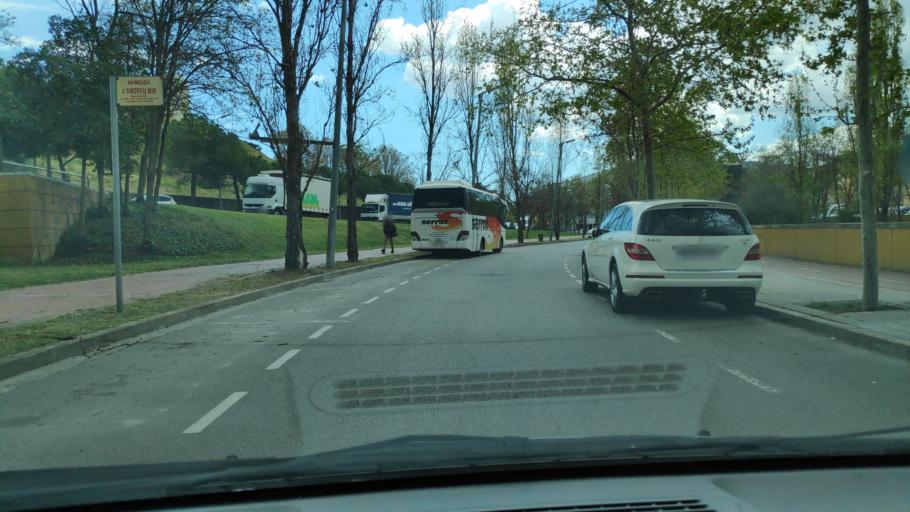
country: ES
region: Catalonia
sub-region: Provincia de Barcelona
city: Sant Quirze del Valles
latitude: 41.5512
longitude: 2.0892
